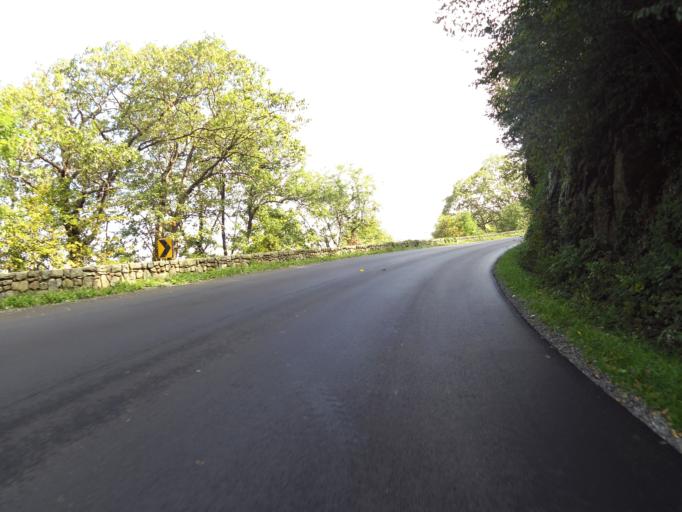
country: US
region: Virginia
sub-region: Page County
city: Luray
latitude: 38.6562
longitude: -78.3132
